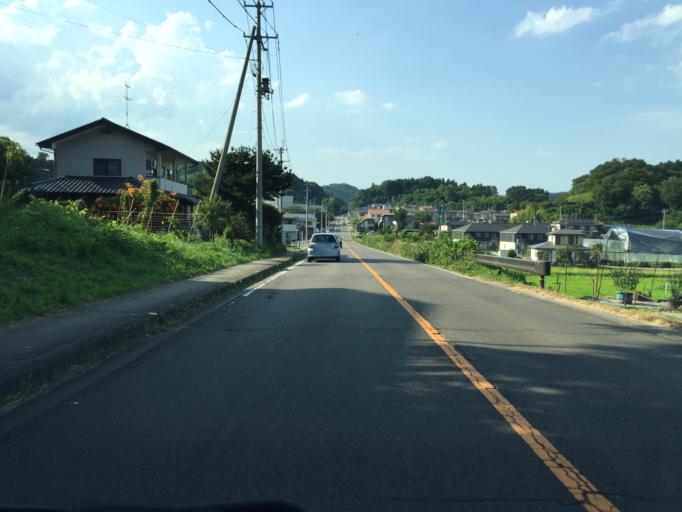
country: JP
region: Fukushima
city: Nihommatsu
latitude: 37.5766
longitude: 140.4171
